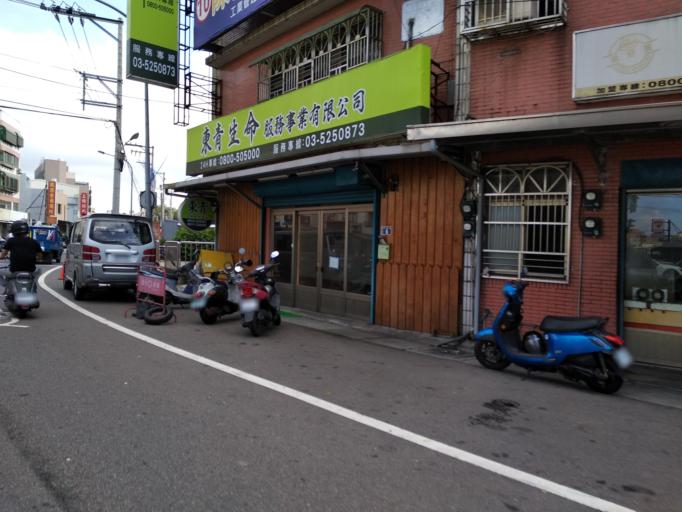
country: TW
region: Taiwan
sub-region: Hsinchu
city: Hsinchu
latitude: 24.7951
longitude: 120.9560
